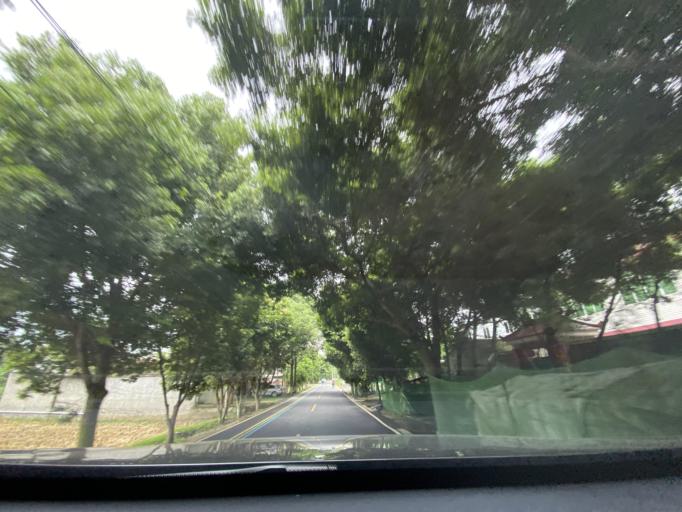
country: CN
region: Sichuan
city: Dongsheng
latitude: 30.4085
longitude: 103.9984
